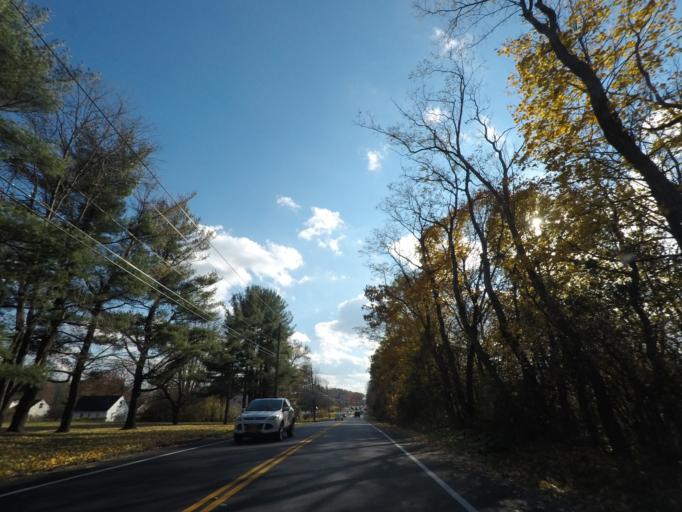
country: US
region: New York
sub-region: Schenectady County
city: Niskayuna
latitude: 42.7866
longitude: -73.8931
